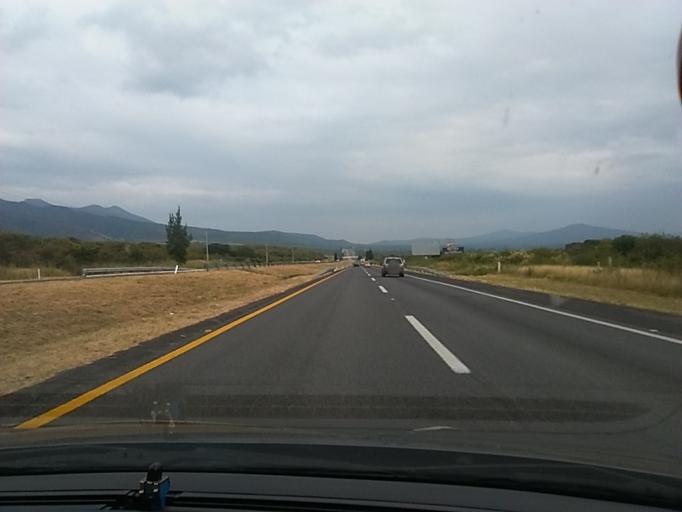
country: MX
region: Michoacan
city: Churintzio
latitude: 20.1428
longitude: -102.0839
